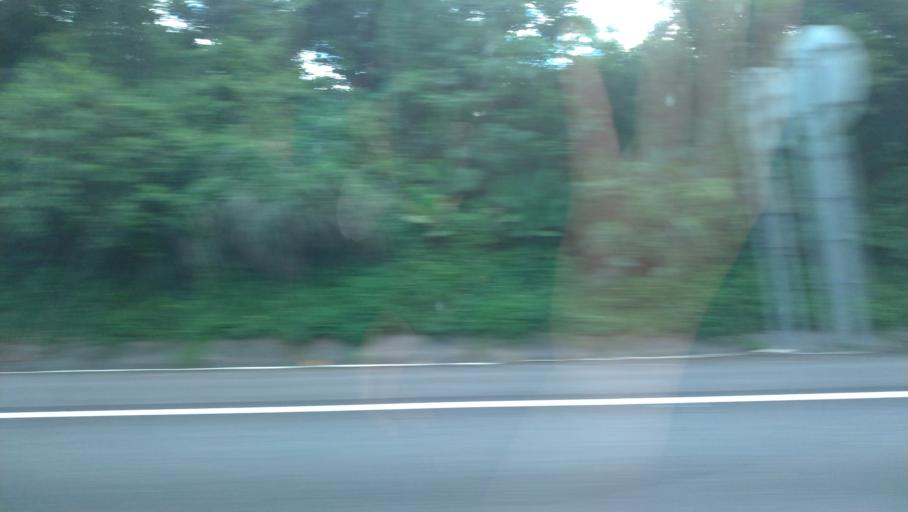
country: TW
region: Taiwan
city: Daxi
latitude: 24.8157
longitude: 121.2005
